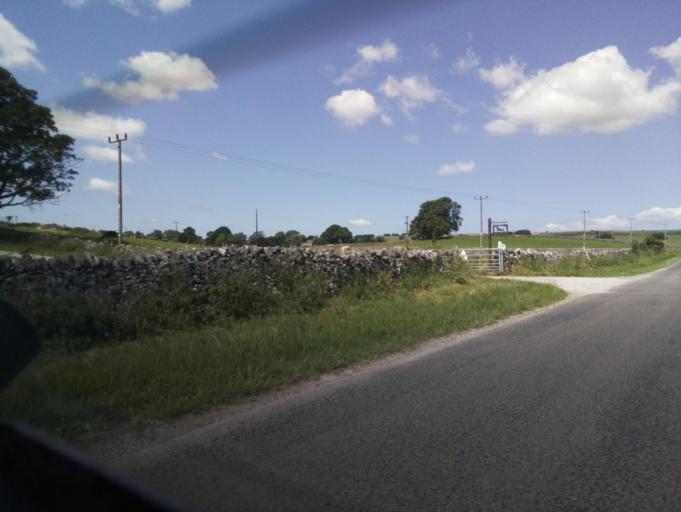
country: GB
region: England
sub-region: Derbyshire
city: Tideswell
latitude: 53.2099
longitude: -1.7809
